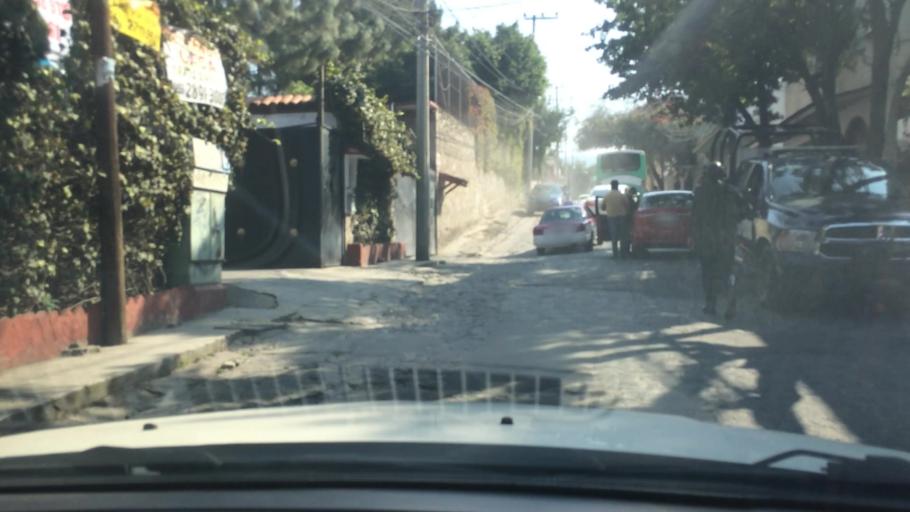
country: MX
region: Mexico City
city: Tlalpan
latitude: 19.2628
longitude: -99.1727
